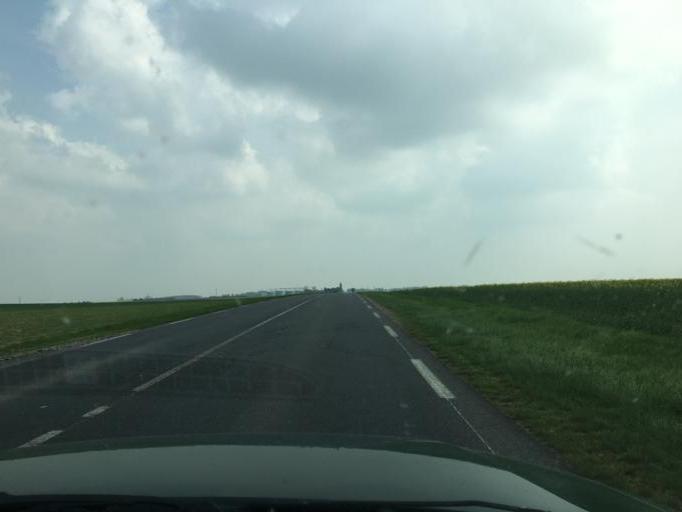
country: FR
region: Centre
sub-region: Departement du Loir-et-Cher
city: Ouzouer-le-Marche
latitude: 47.9074
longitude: 1.4954
